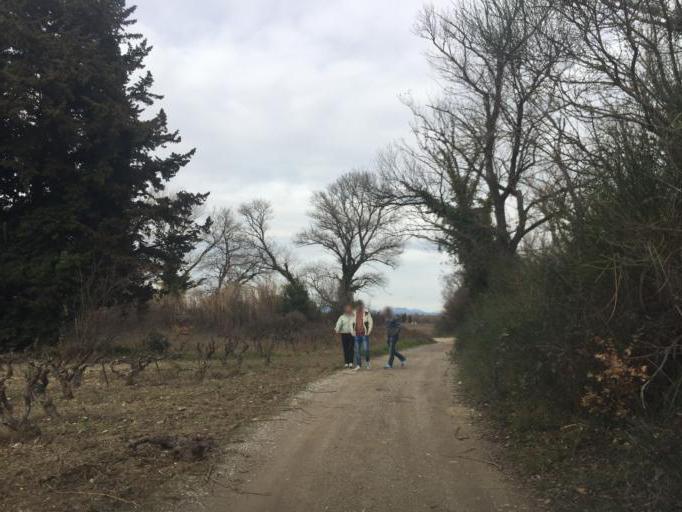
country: FR
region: Provence-Alpes-Cote d'Azur
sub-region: Departement du Vaucluse
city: Violes
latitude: 44.1622
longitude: 4.9600
